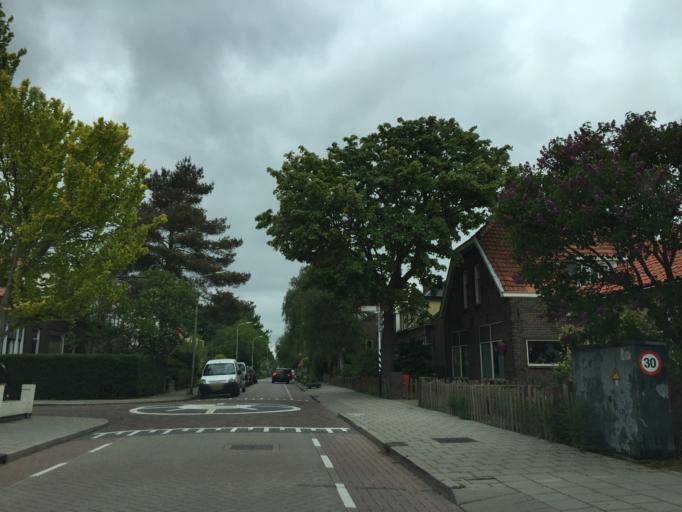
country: NL
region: South Holland
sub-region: Gemeente Pijnacker-Nootdorp
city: Pijnacker
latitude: 52.0104
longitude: 4.3951
